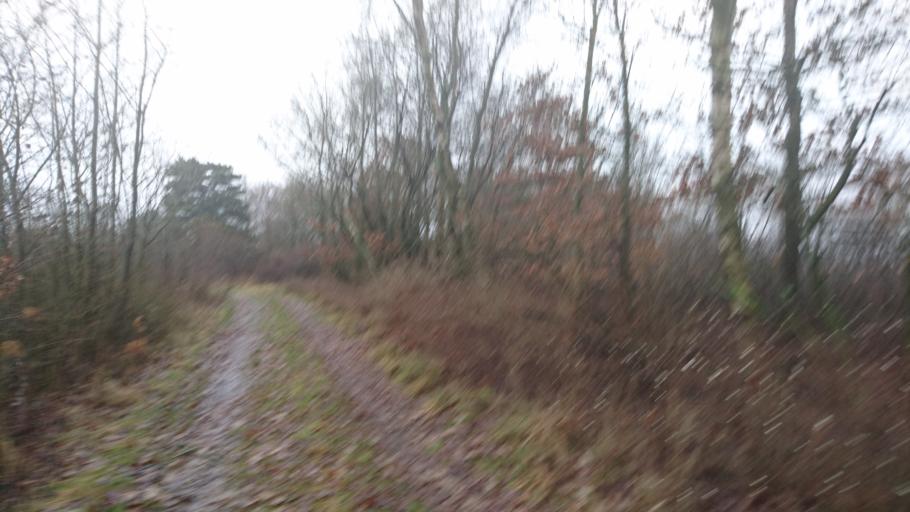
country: DK
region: Central Jutland
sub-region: Herning Kommune
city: Sunds
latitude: 56.1968
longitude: 9.0269
